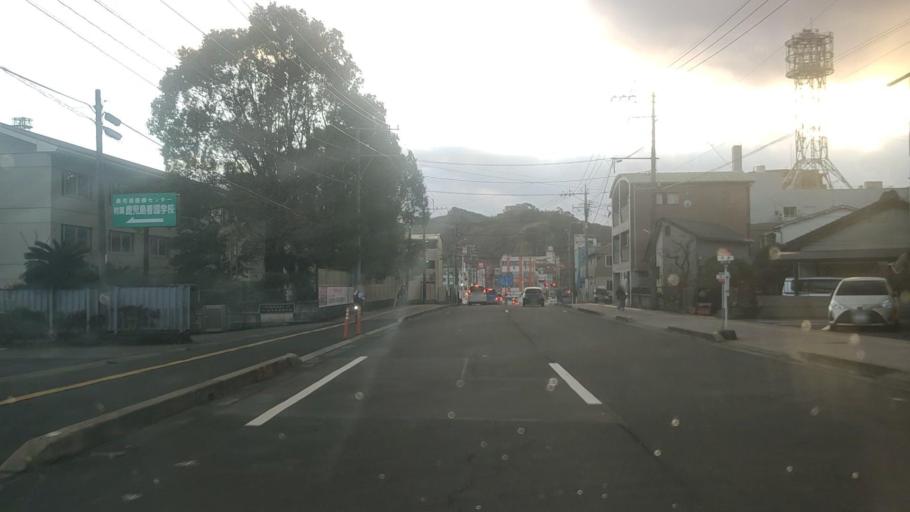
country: JP
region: Kagoshima
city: Kagoshima-shi
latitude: 31.6162
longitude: 130.5318
